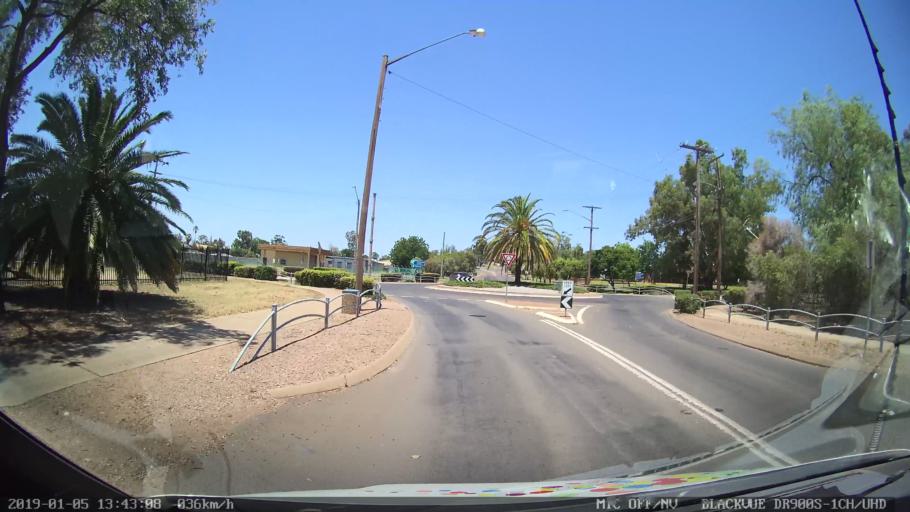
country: AU
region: New South Wales
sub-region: Gunnedah
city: Gunnedah
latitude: -30.9811
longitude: 150.2507
